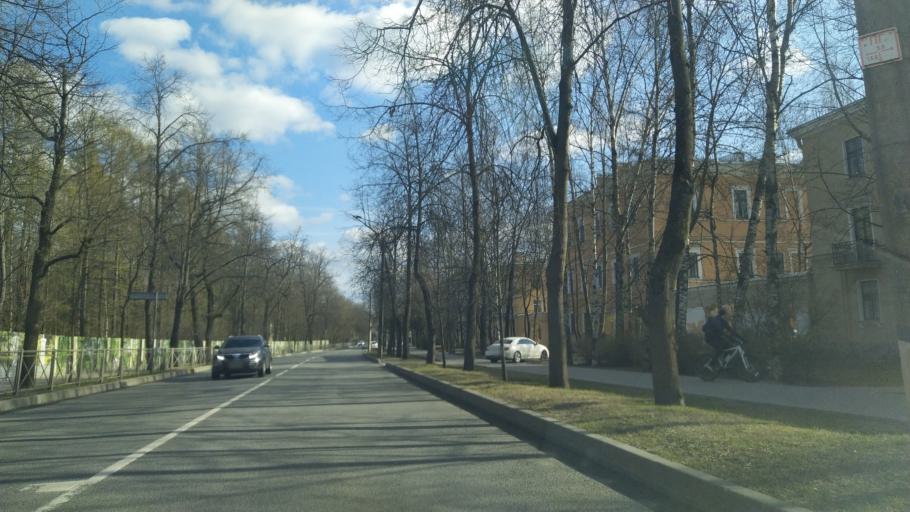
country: RU
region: St.-Petersburg
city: Pushkin
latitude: 59.7087
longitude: 30.4146
